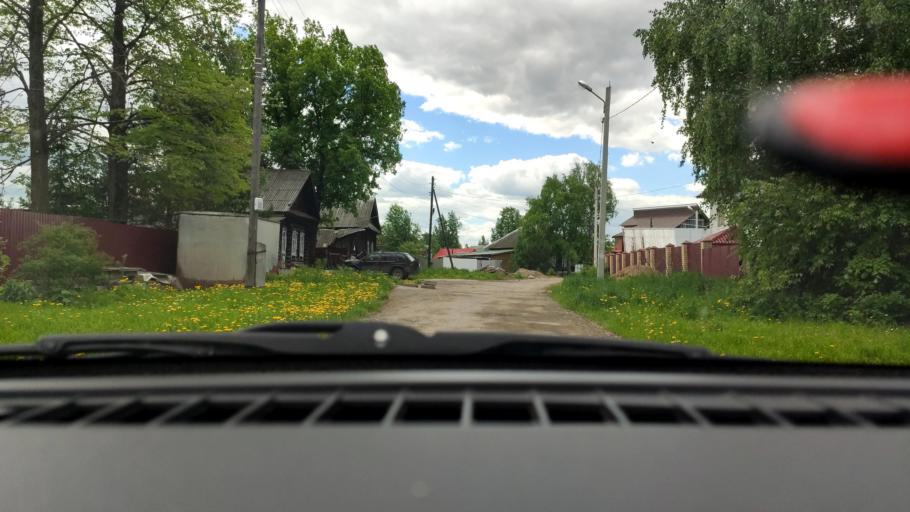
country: RU
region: Perm
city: Perm
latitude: 58.0466
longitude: 56.3617
